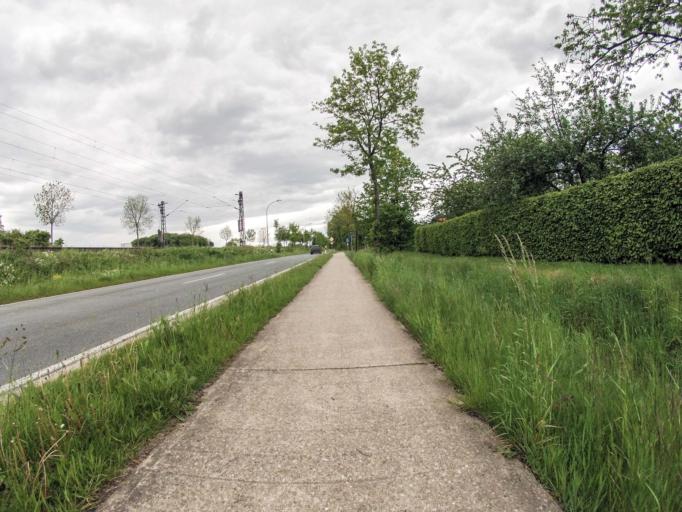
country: DE
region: Lower Saxony
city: Belm
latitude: 52.3294
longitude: 8.1464
